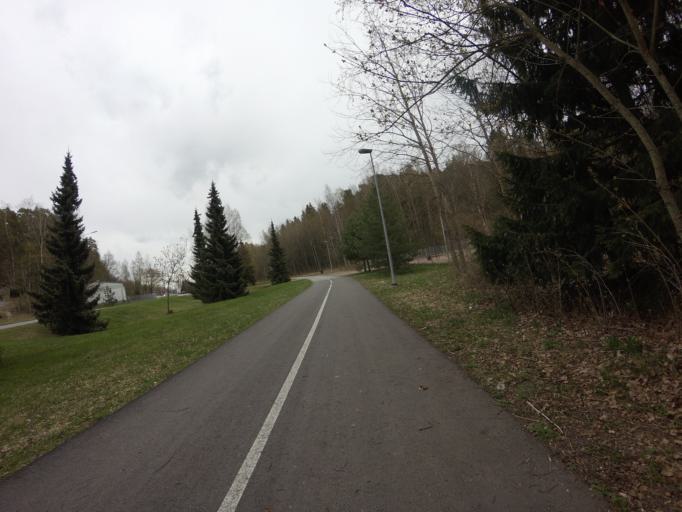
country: FI
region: Varsinais-Suomi
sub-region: Turku
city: Raisio
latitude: 60.4511
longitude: 22.1597
